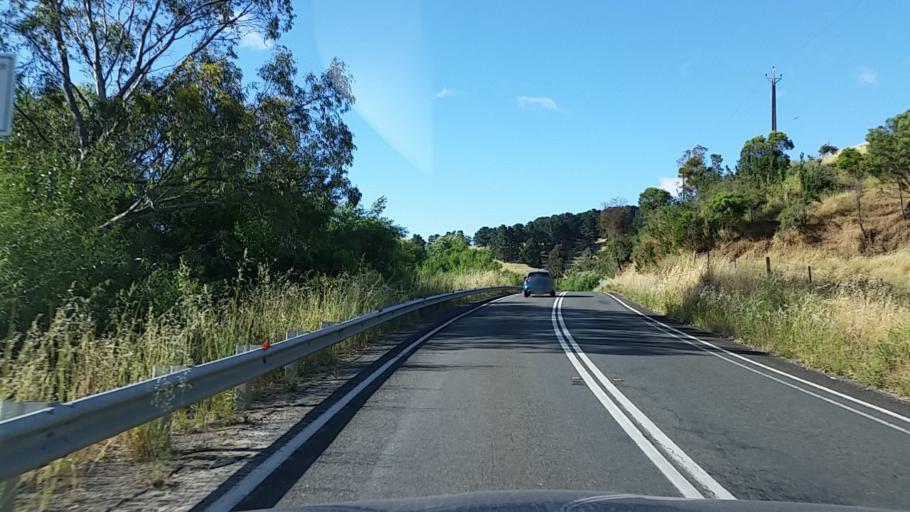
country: AU
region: South Australia
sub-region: Mount Barker
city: Meadows
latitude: -35.2402
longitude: 138.7651
